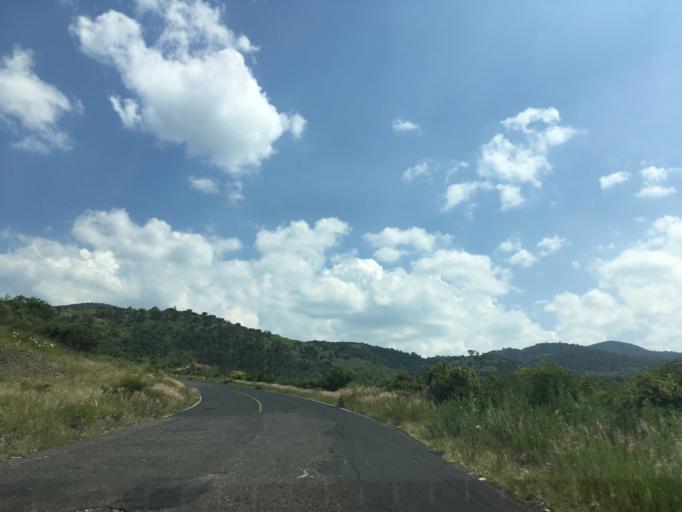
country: MX
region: Michoacan
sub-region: Morelia
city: Morelos
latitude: 19.6452
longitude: -101.2047
